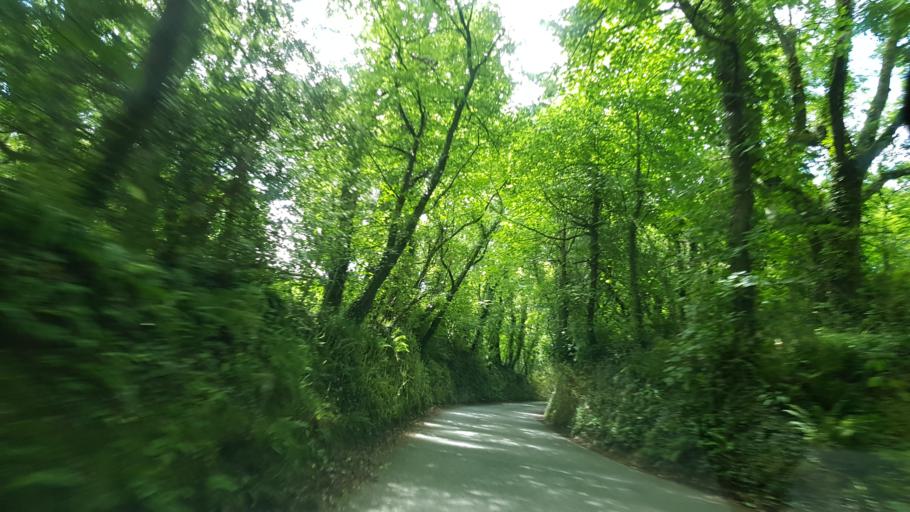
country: GB
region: Wales
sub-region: Pembrokeshire
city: Haverfordwest
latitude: 51.8208
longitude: -4.9404
